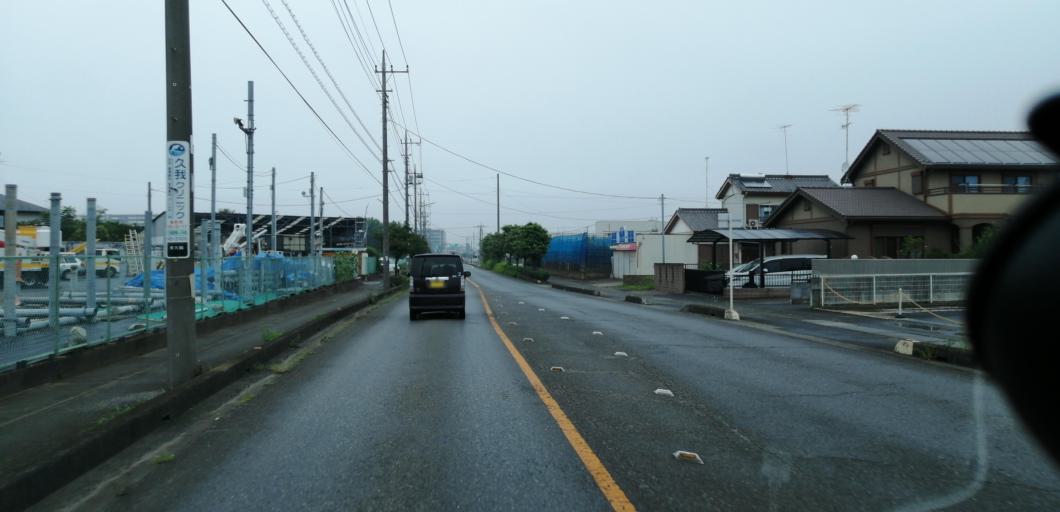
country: JP
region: Saitama
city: Kukichuo
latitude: 36.0891
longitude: 139.6870
